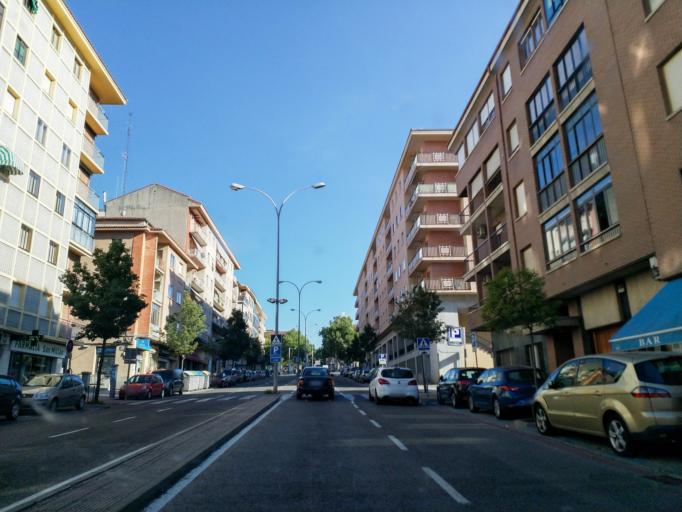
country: ES
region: Castille and Leon
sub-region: Provincia de Segovia
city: Segovia
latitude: 40.9458
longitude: -4.1226
